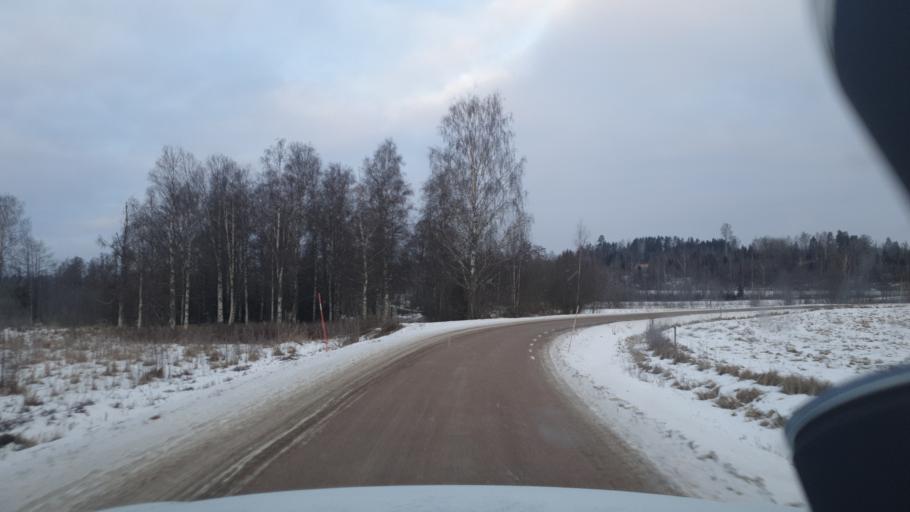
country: SE
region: Vaermland
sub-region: Eda Kommun
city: Amotfors
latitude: 59.8283
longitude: 12.3583
